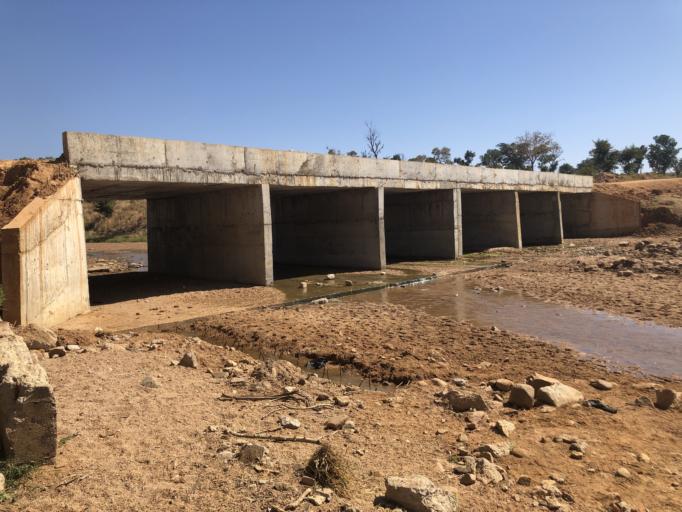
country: NG
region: Adamawa
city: Toungo
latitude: 8.1427
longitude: 11.9901
